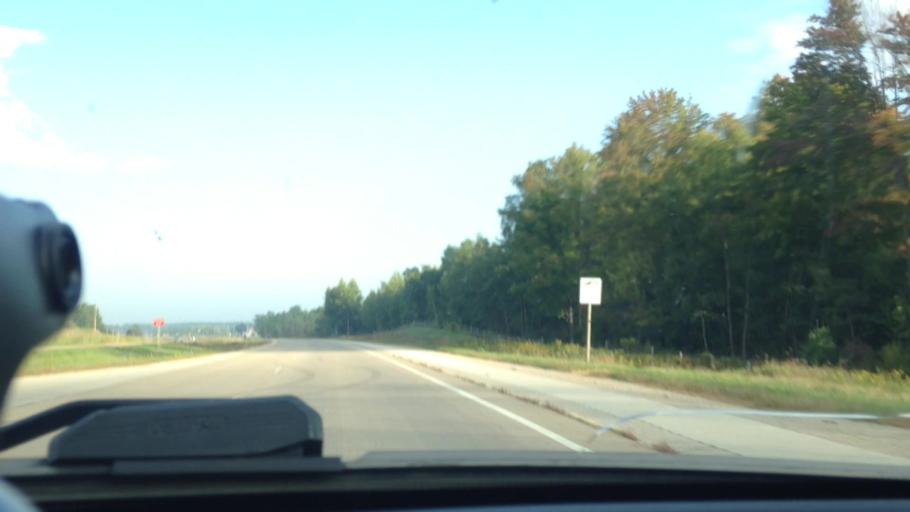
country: US
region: Wisconsin
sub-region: Oconto County
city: Oconto Falls
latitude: 44.9725
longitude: -88.0378
